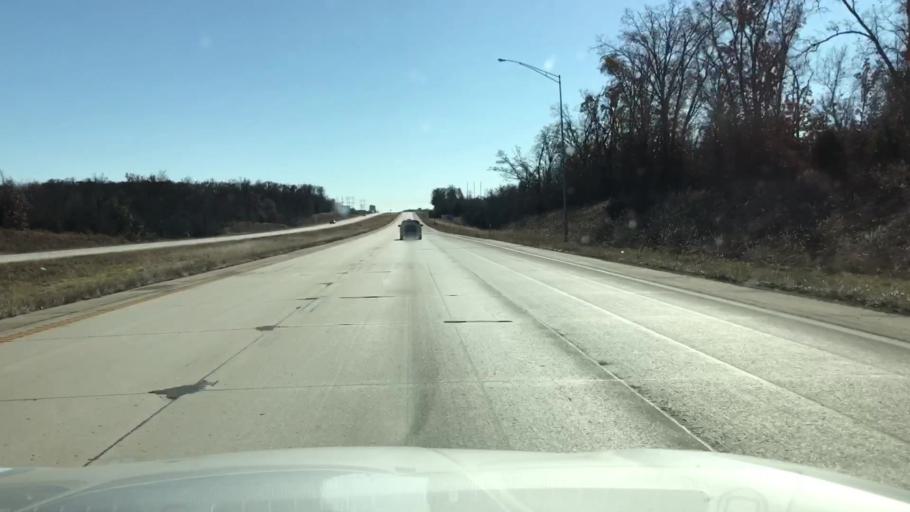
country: US
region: Missouri
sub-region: Jasper County
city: Duenweg
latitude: 37.0494
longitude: -94.4273
